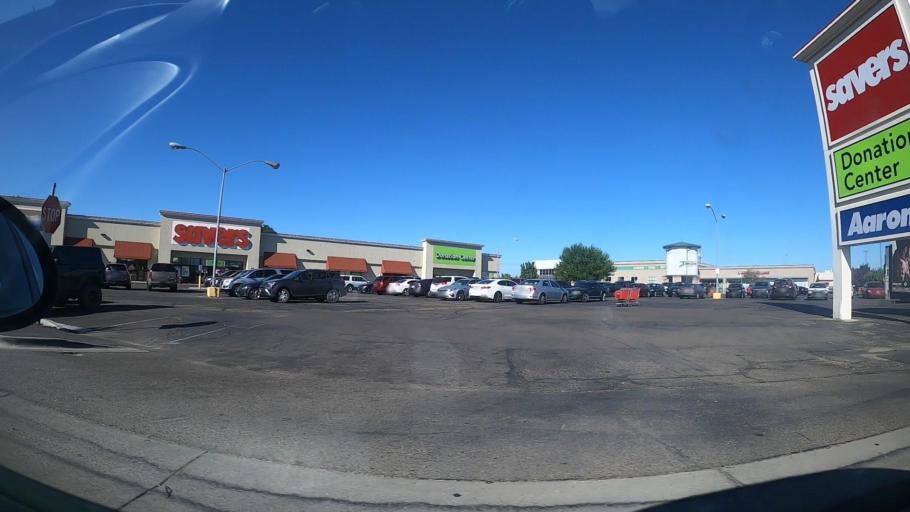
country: US
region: Idaho
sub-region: Canyon County
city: Nampa
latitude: 43.6026
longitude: -116.5988
